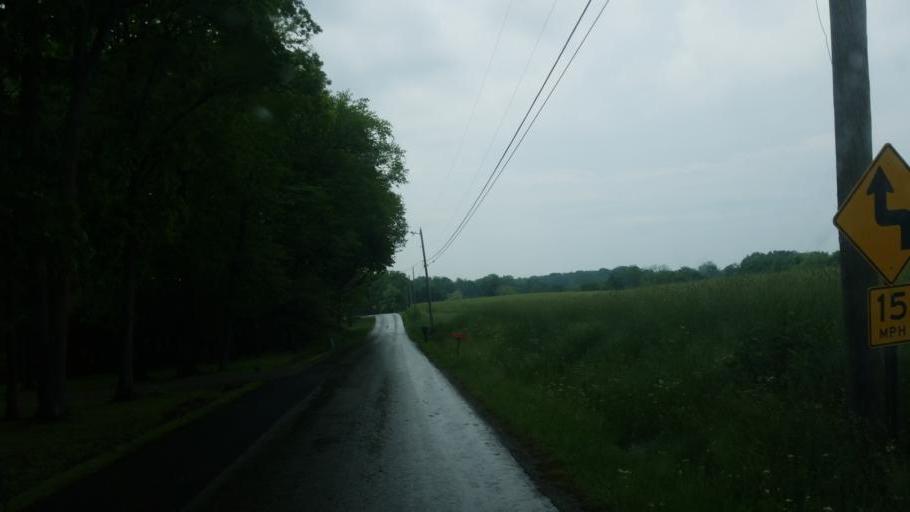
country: US
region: Ohio
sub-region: Wayne County
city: Dalton
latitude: 40.7923
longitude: -81.7141
